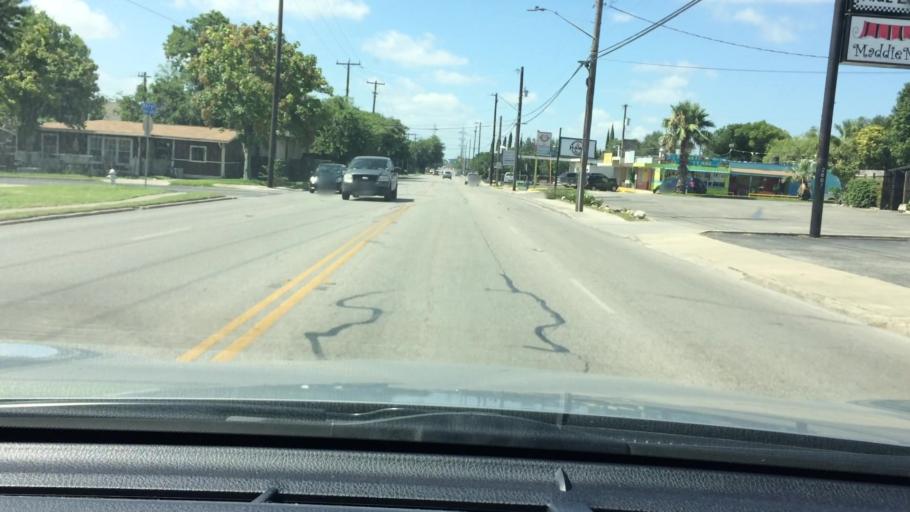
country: US
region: Texas
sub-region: Bexar County
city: Balcones Heights
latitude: 29.4979
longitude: -98.5351
